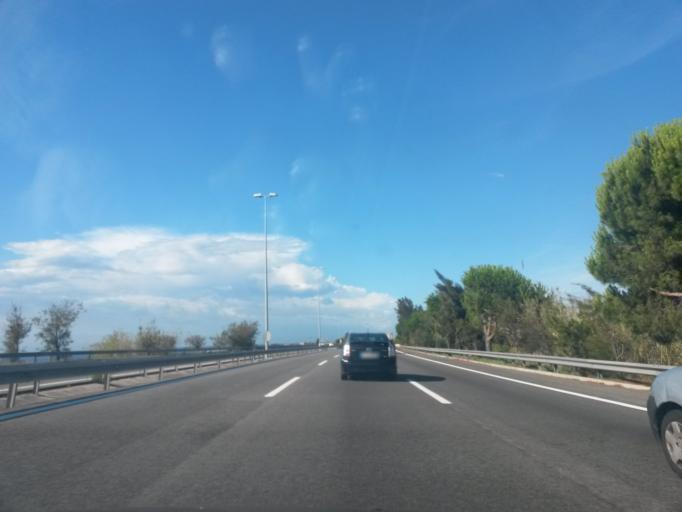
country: ES
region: Catalonia
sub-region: Provincia de Barcelona
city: Cabrera de Mar
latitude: 41.5259
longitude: 2.4105
